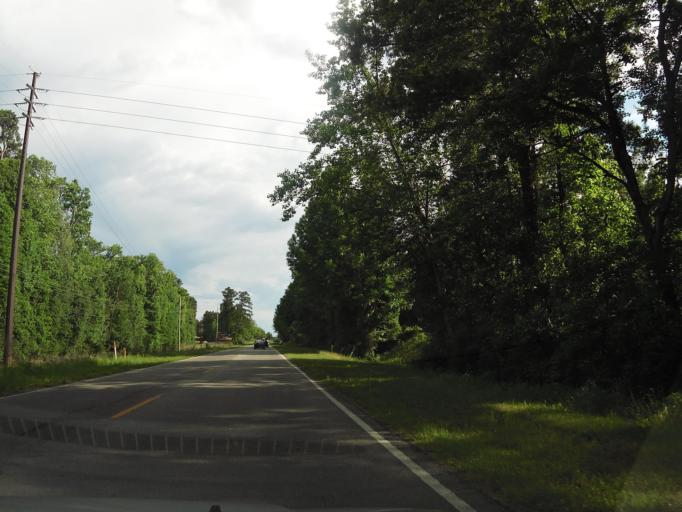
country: US
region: South Carolina
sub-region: Hampton County
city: Estill
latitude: 32.7709
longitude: -81.2410
